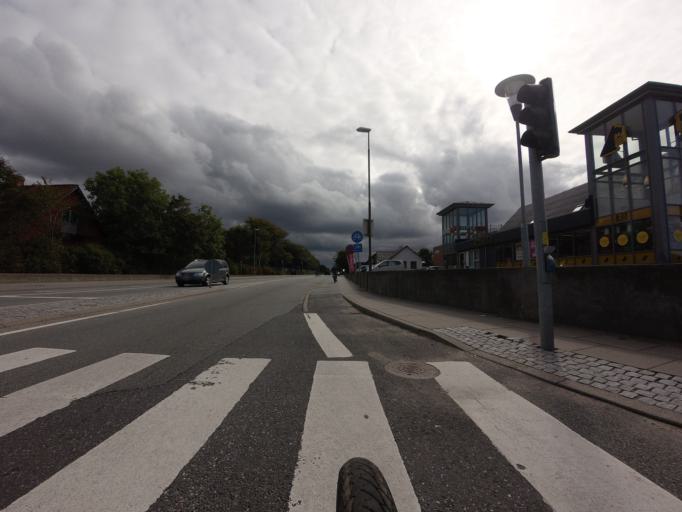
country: DK
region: North Denmark
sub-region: Hjorring Kommune
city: Hjorring
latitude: 57.4823
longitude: 9.9918
